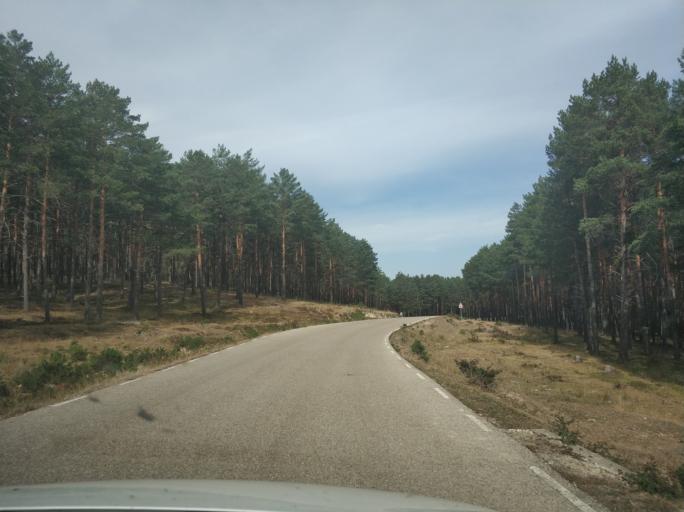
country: ES
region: Castille and Leon
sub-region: Provincia de Soria
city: Navaleno
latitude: 41.8629
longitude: -2.9405
